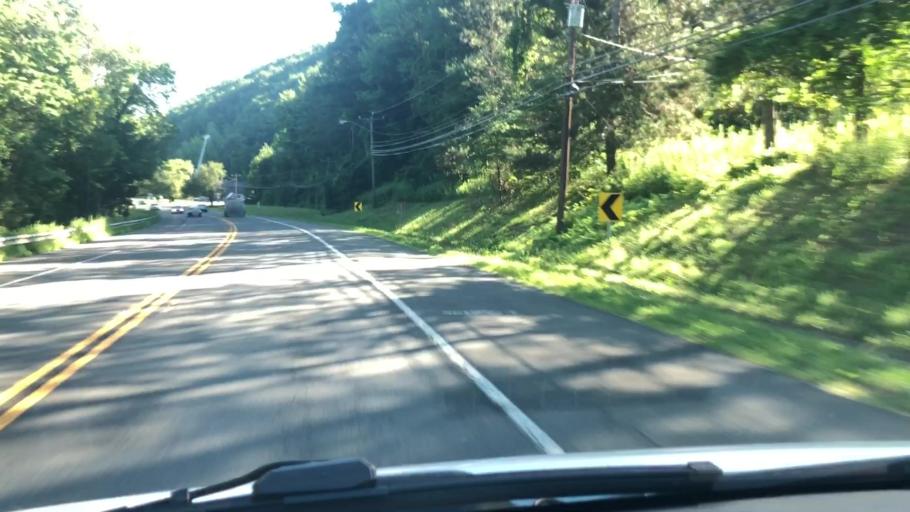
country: US
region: Massachusetts
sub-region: Berkshire County
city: Lanesborough
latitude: 42.4984
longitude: -73.1972
